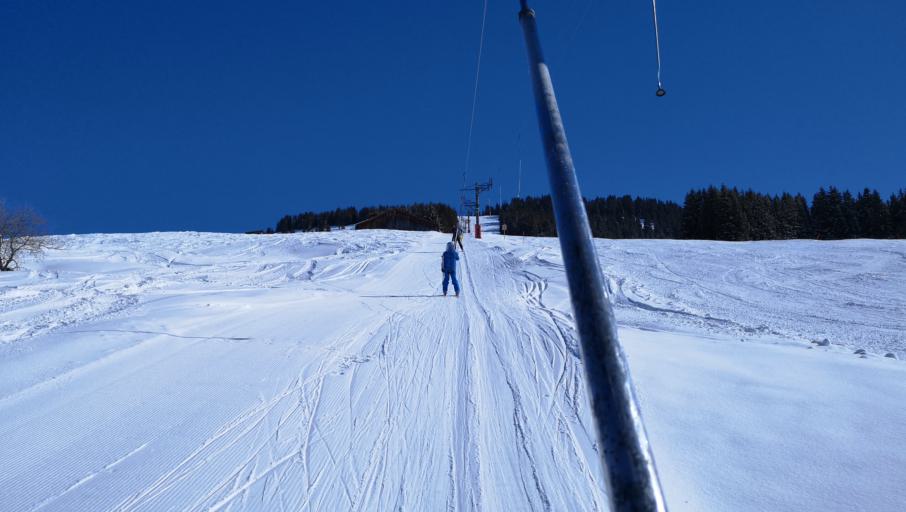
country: FR
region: Rhone-Alpes
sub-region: Departement de la Haute-Savoie
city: Megeve
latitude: 45.8449
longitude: 6.6556
